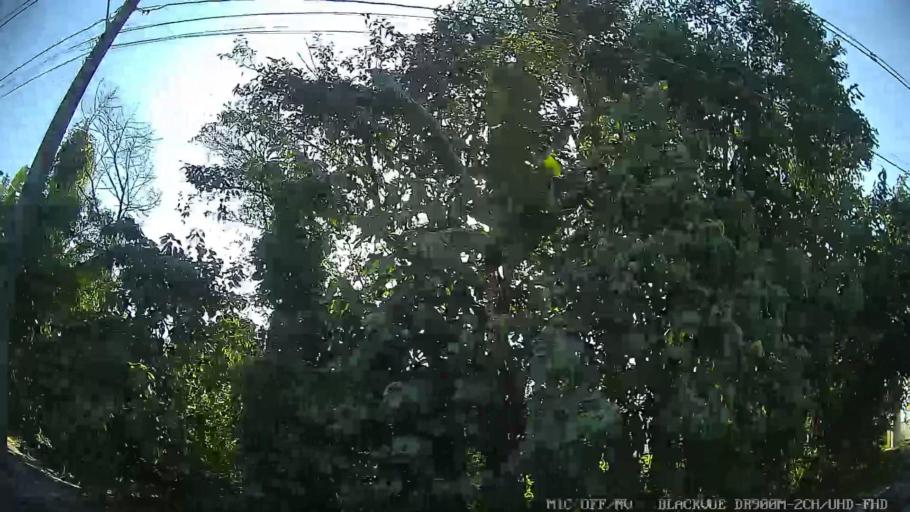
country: BR
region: Sao Paulo
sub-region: Guaruja
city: Guaruja
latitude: -23.9716
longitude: -46.2170
